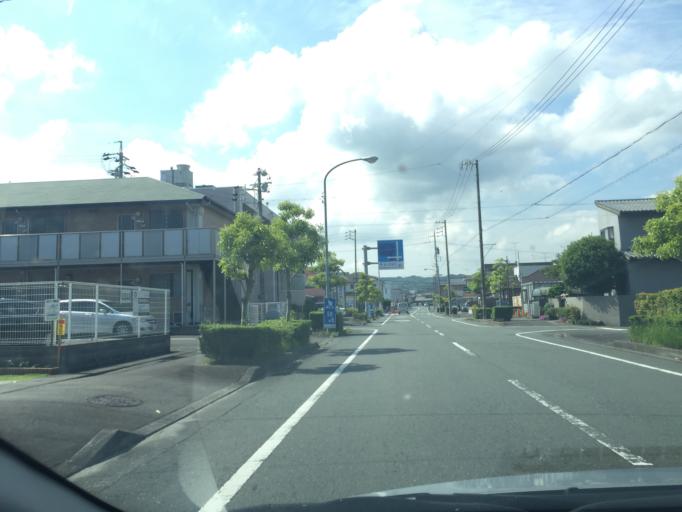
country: JP
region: Shizuoka
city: Kakegawa
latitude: 34.7740
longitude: 138.0031
